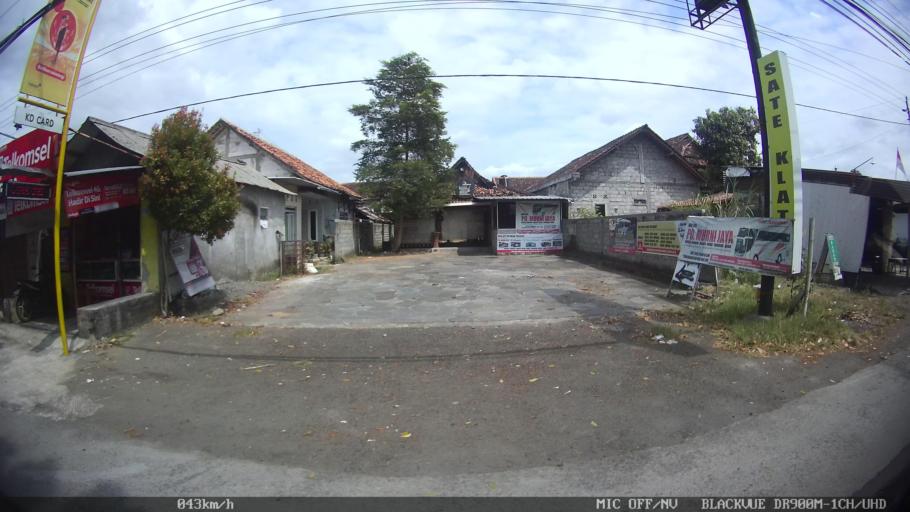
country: ID
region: Central Java
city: Candi Prambanan
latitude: -7.7905
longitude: 110.4827
